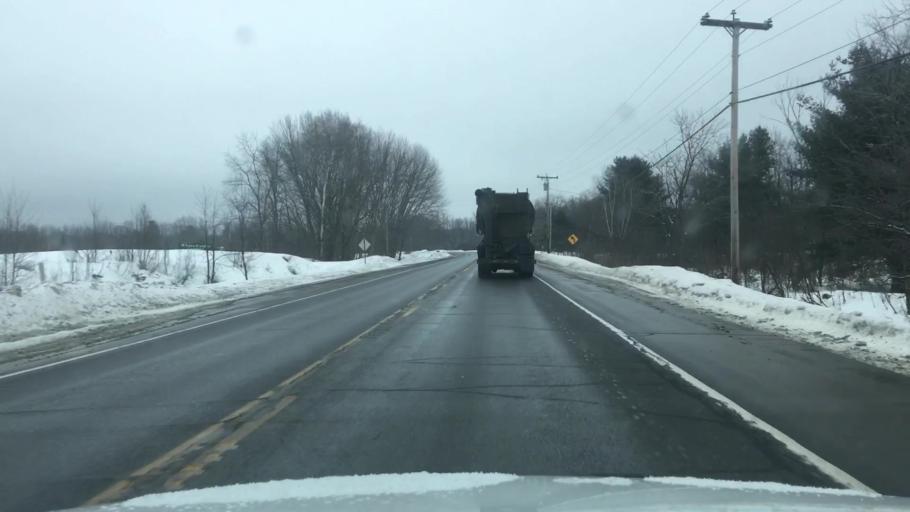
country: US
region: Maine
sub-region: Franklin County
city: New Sharon
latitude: 44.6373
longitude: -70.0476
